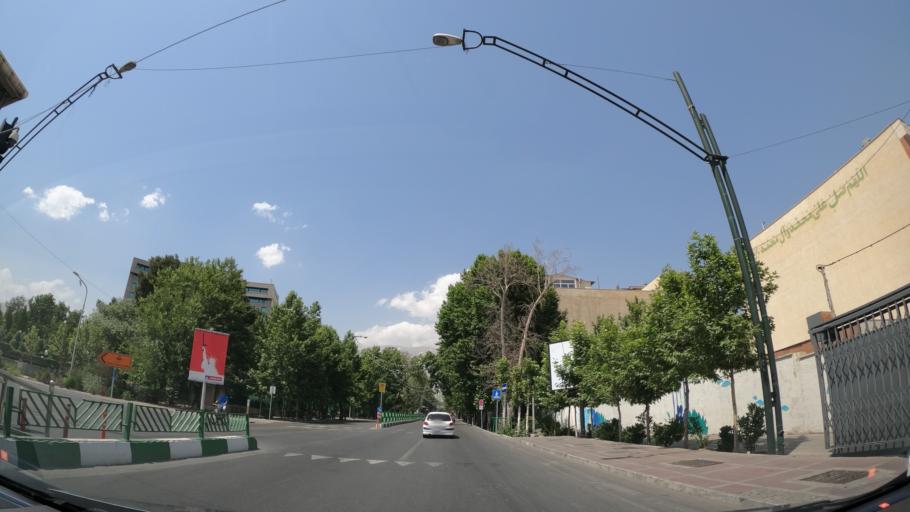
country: IR
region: Tehran
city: Tajrish
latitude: 35.7859
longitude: 51.4152
